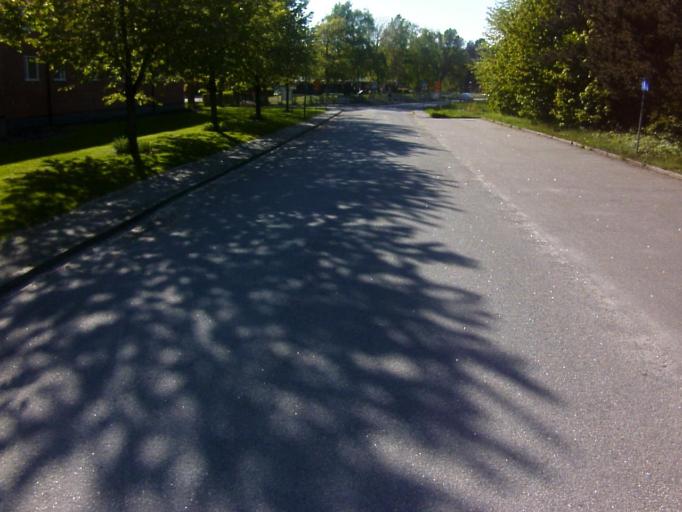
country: SE
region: Blekinge
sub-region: Solvesborgs Kommun
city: Soelvesborg
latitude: 56.0382
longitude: 14.5716
